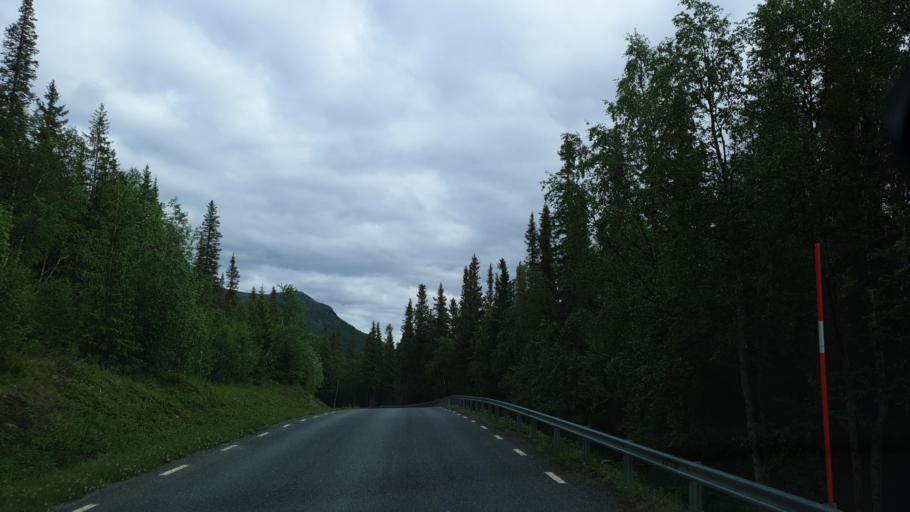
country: SE
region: Vaesterbotten
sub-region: Vilhelmina Kommun
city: Sjoberg
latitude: 65.2566
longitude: 15.4045
